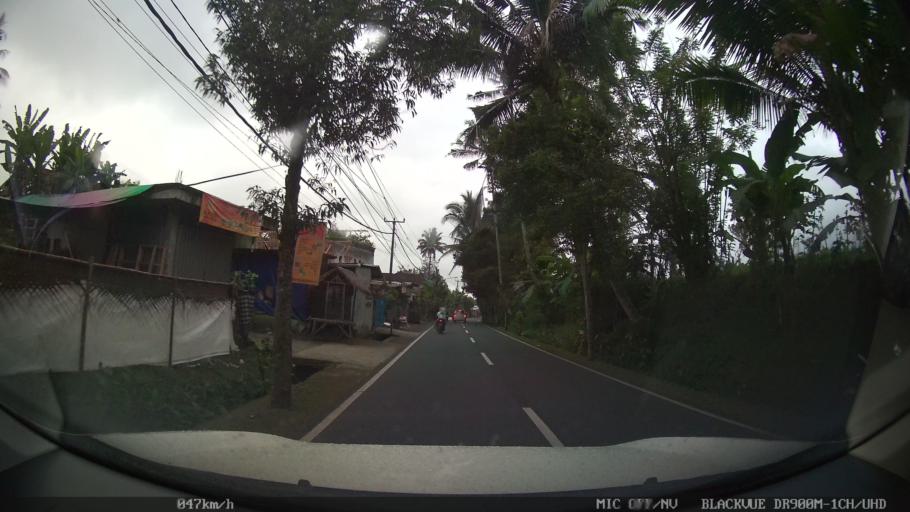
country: ID
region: Bali
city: Badung
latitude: -8.4171
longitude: 115.2447
